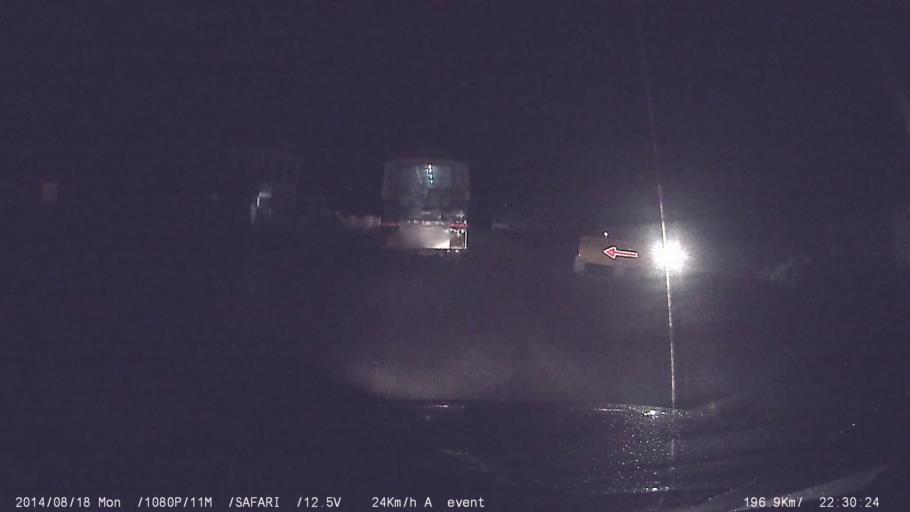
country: IN
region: Kerala
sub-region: Thrissur District
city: Chelakara
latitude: 10.6048
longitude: 76.4934
